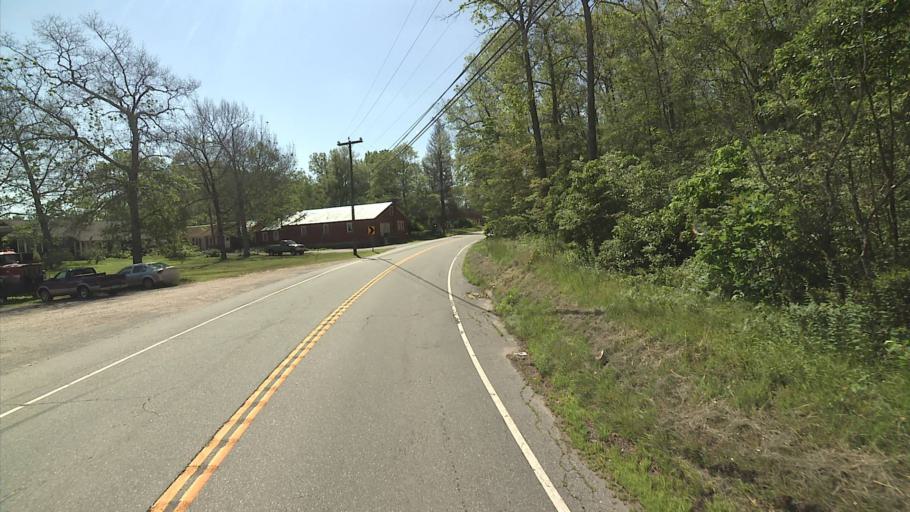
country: US
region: Connecticut
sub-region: Windham County
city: Moosup
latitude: 41.7171
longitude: -71.8469
